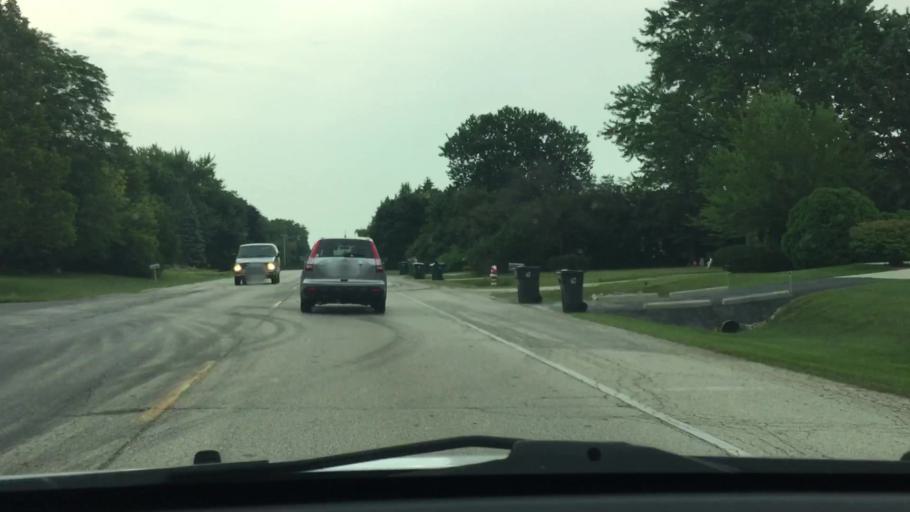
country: US
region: Wisconsin
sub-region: Waukesha County
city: New Berlin
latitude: 42.9955
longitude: -88.0960
